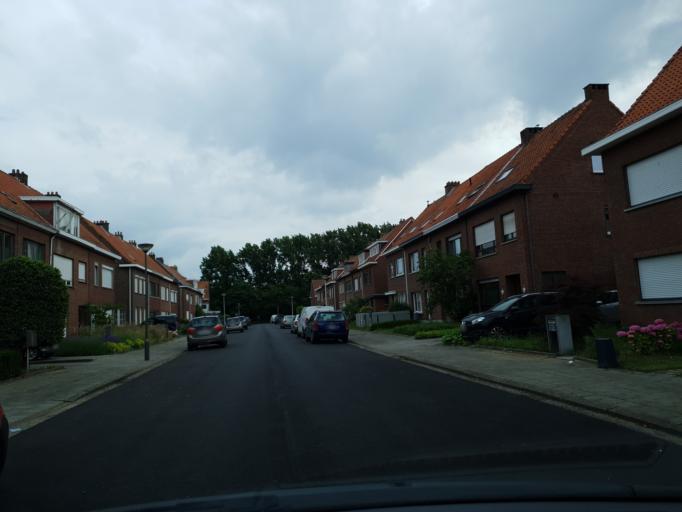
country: BE
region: Flanders
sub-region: Provincie Antwerpen
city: Kapellen
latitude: 51.2761
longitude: 4.4090
